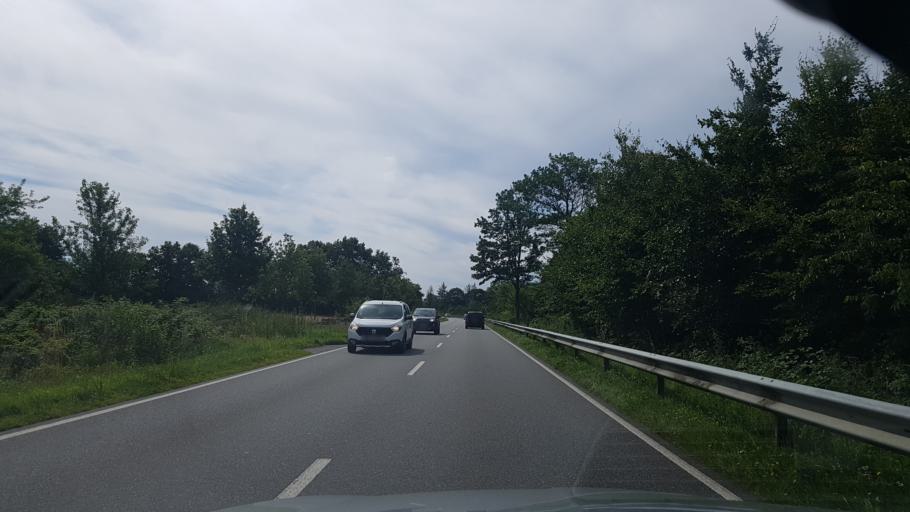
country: DE
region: Schleswig-Holstein
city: Osterby
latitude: 54.8219
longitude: 9.2218
